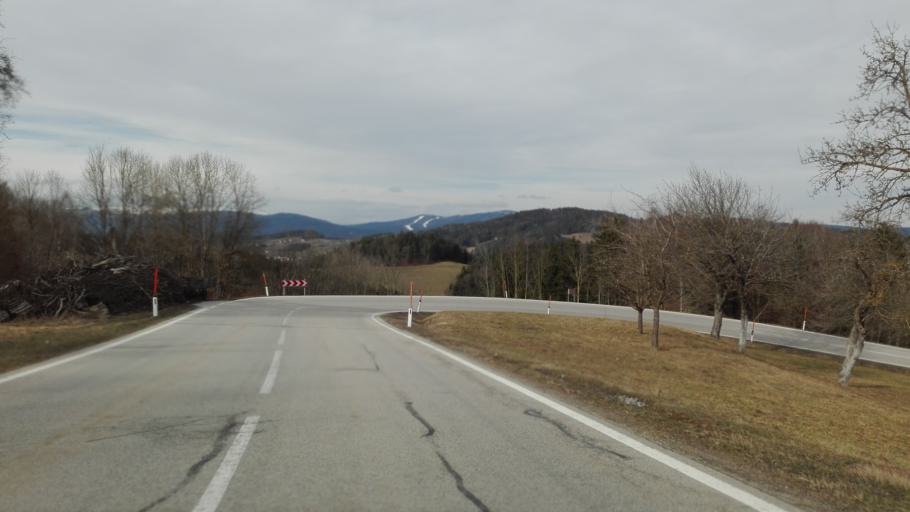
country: AT
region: Upper Austria
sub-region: Politischer Bezirk Rohrbach
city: Nebelberg
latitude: 48.6235
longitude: 13.8762
